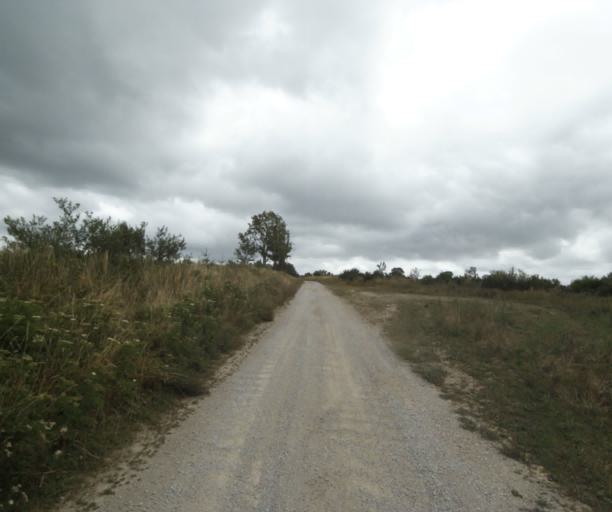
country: FR
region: Midi-Pyrenees
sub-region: Departement du Tarn
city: Soreze
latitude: 43.4251
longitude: 2.1208
